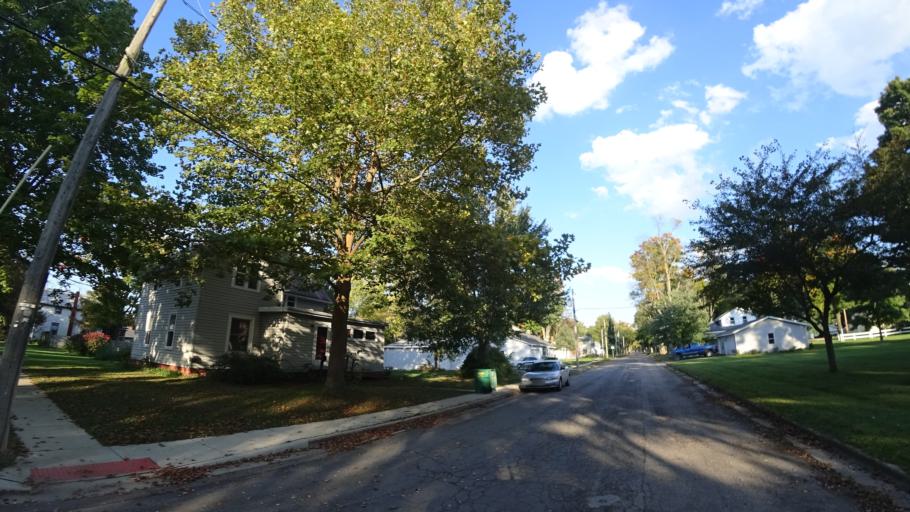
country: US
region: Michigan
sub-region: Saint Joseph County
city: Three Rivers
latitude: 41.9537
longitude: -85.6386
